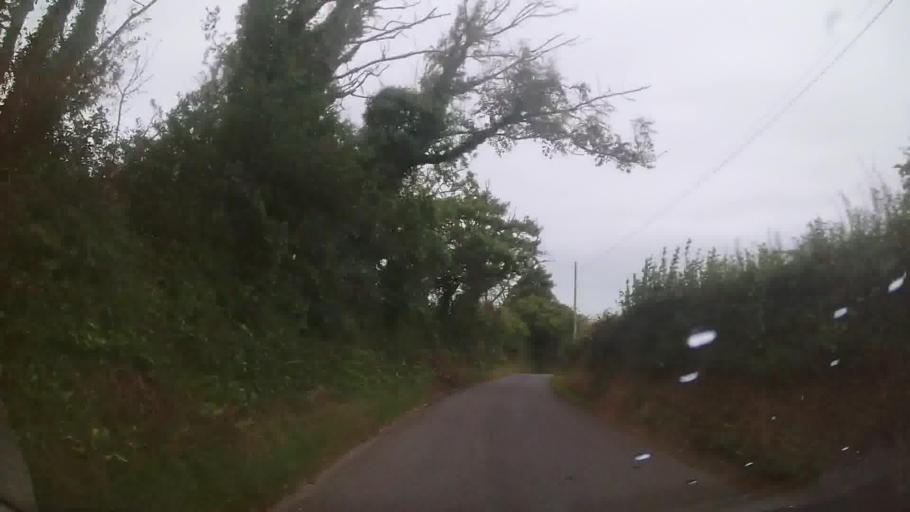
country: GB
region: Wales
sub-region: Pembrokeshire
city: Saundersfoot
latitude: 51.7431
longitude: -4.6599
